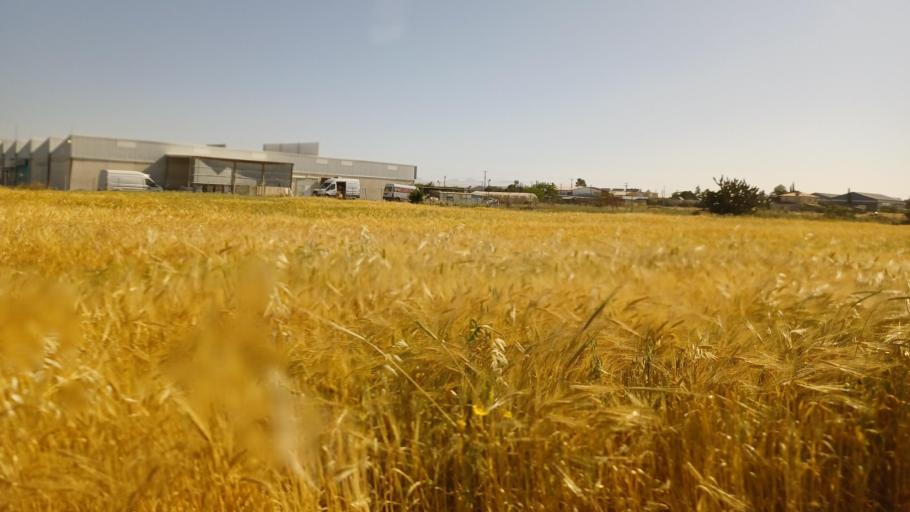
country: CY
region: Lefkosia
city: Kokkinotrimithia
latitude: 35.1474
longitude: 33.2170
